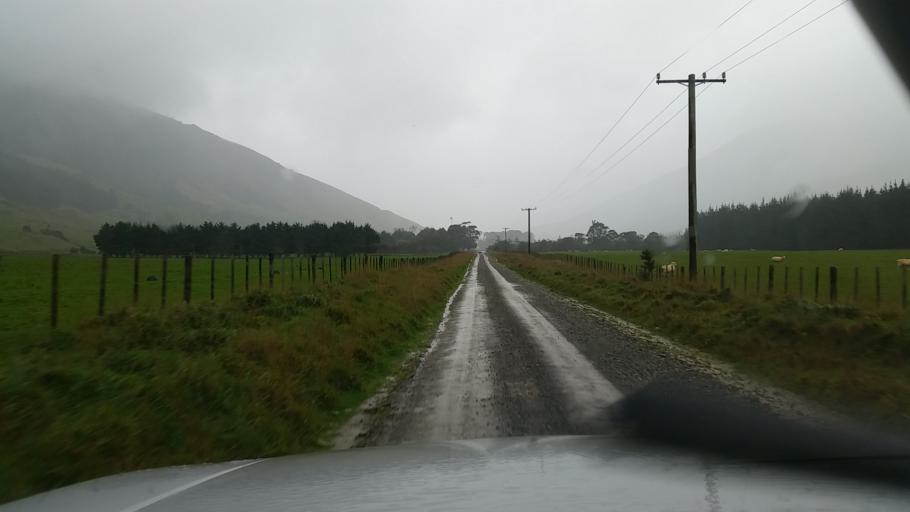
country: NZ
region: Marlborough
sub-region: Marlborough District
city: Picton
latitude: -41.1261
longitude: 174.0398
